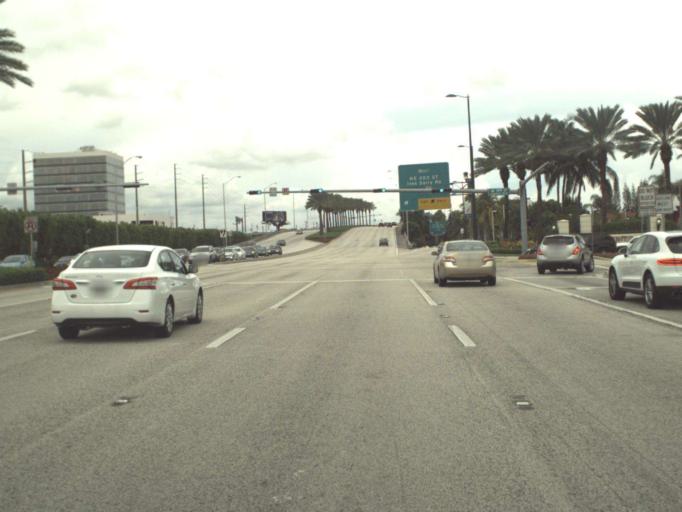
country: US
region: Florida
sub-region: Miami-Dade County
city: Aventura
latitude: 25.9593
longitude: -80.1468
